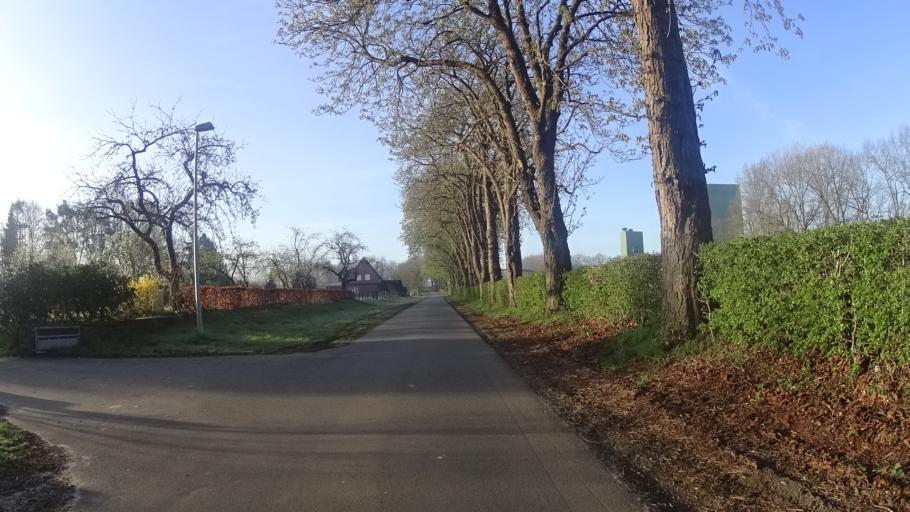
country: DE
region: Lower Saxony
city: Fresenburg
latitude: 52.8876
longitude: 7.3143
